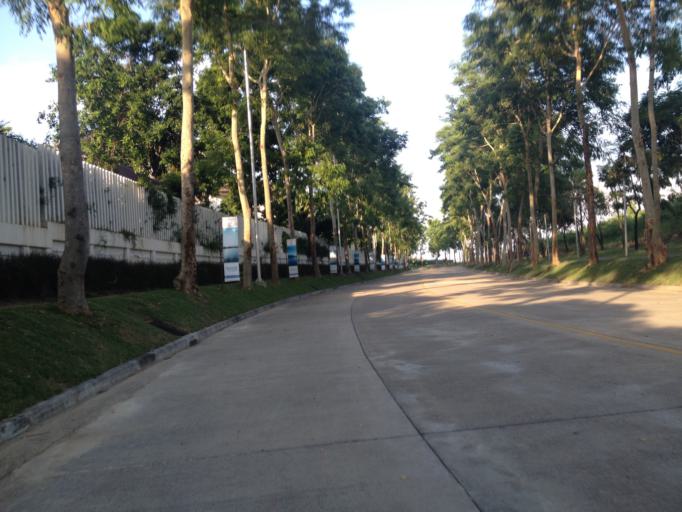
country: TH
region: Chiang Mai
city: Chiang Mai
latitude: 18.7523
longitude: 98.9472
